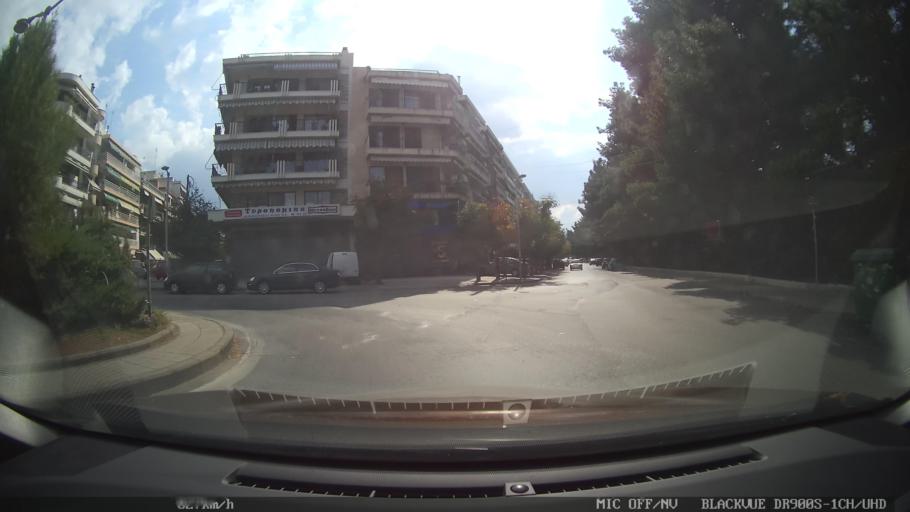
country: GR
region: Central Macedonia
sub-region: Nomos Thessalonikis
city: Triandria
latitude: 40.6085
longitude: 22.9826
